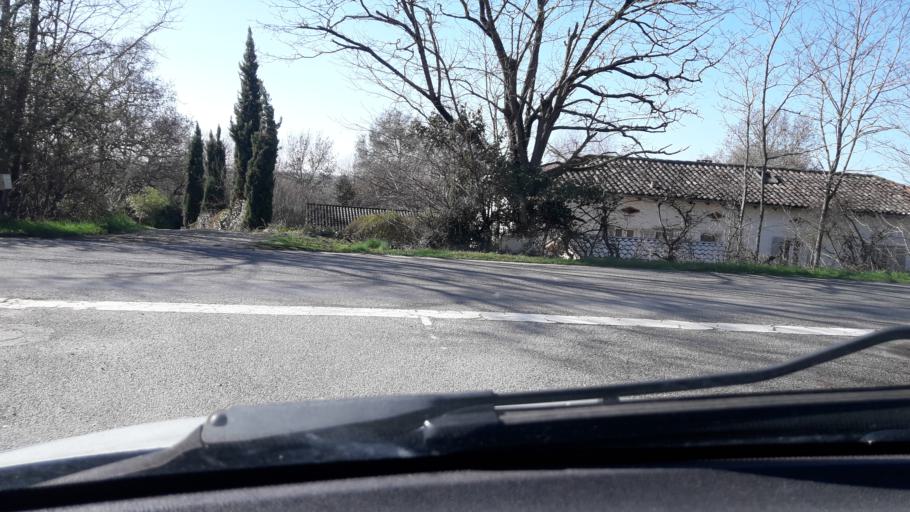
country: FR
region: Midi-Pyrenees
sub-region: Departement du Gers
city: Pujaudran
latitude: 43.6614
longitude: 1.0261
